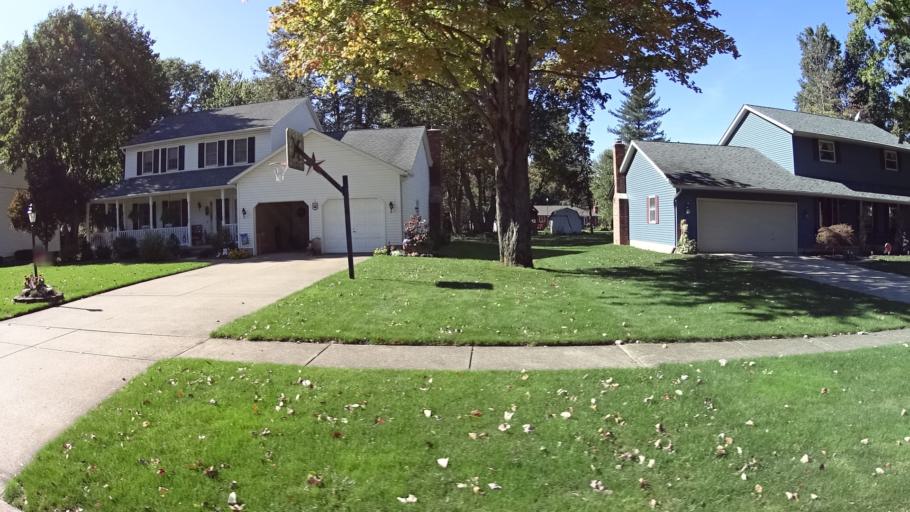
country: US
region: Ohio
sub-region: Lorain County
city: Amherst
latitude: 41.3821
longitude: -82.2175
